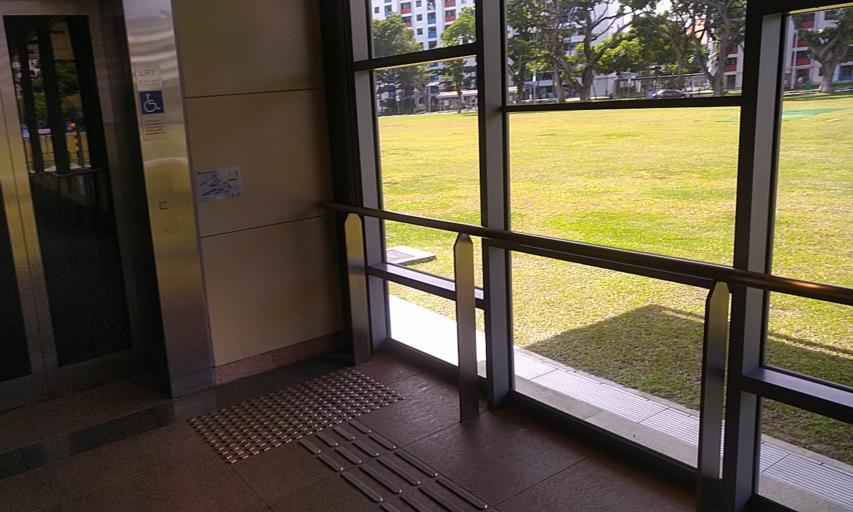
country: SG
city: Singapore
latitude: 1.3267
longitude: 103.8838
